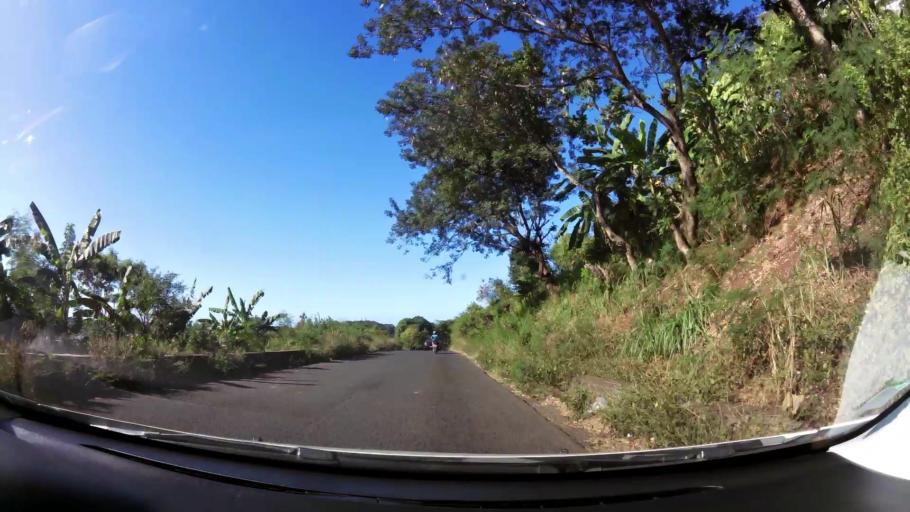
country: YT
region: Mamoudzou
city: Mamoudzou
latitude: -12.7780
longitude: 45.2249
